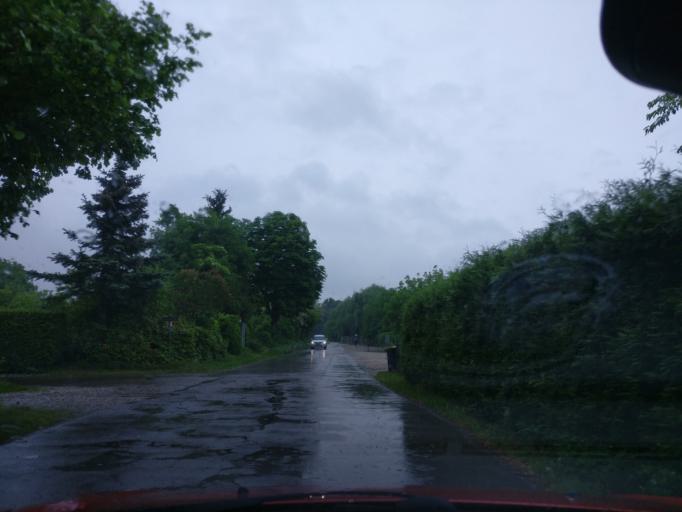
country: DE
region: Bavaria
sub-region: Upper Bavaria
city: Karlsfeld
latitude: 48.2446
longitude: 11.4597
